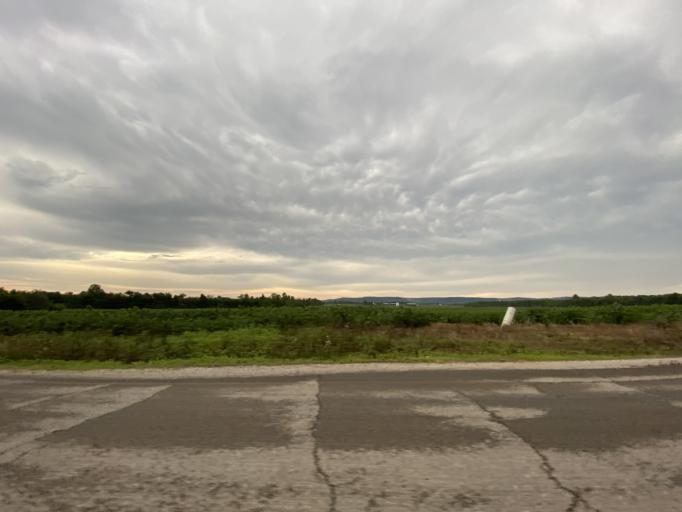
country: US
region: Alabama
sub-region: Lawrence County
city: Moulton
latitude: 34.4640
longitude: -87.4965
